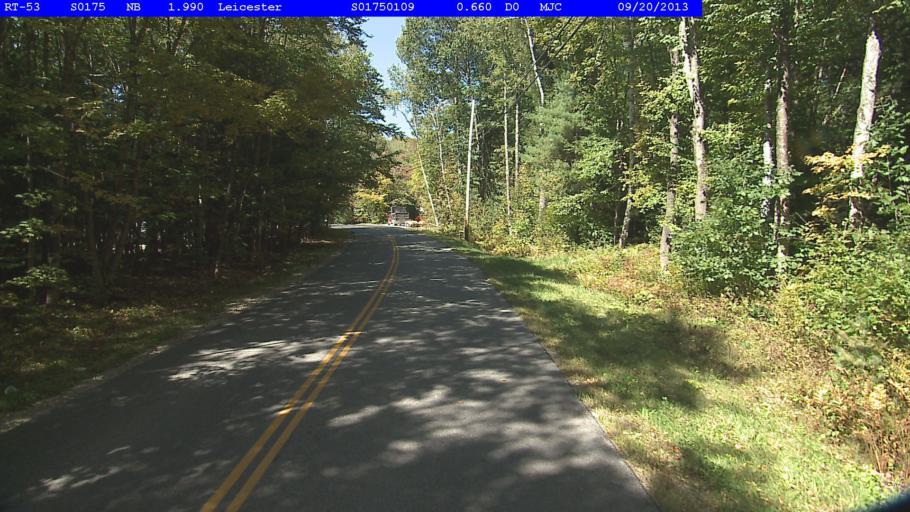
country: US
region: Vermont
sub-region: Rutland County
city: Brandon
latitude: 43.8545
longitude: -73.0630
